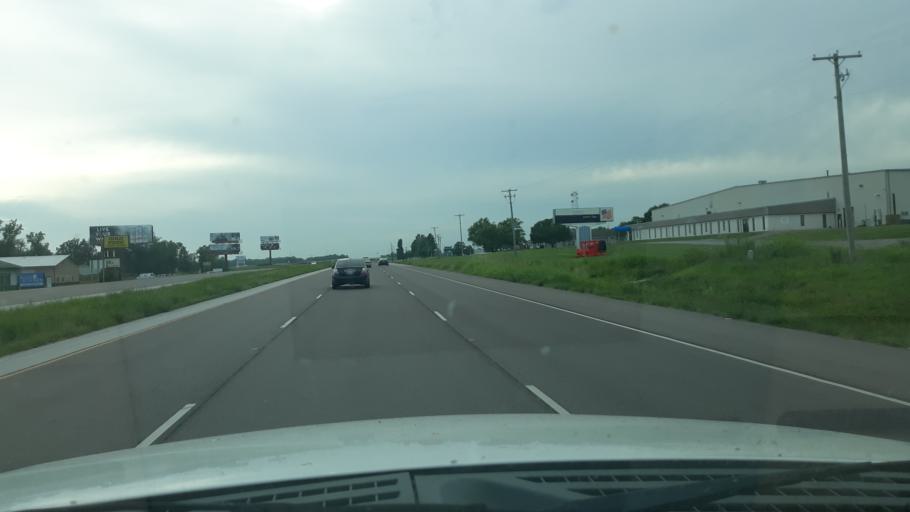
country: US
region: Illinois
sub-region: Williamson County
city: Crainville
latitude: 37.7451
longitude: -89.0461
